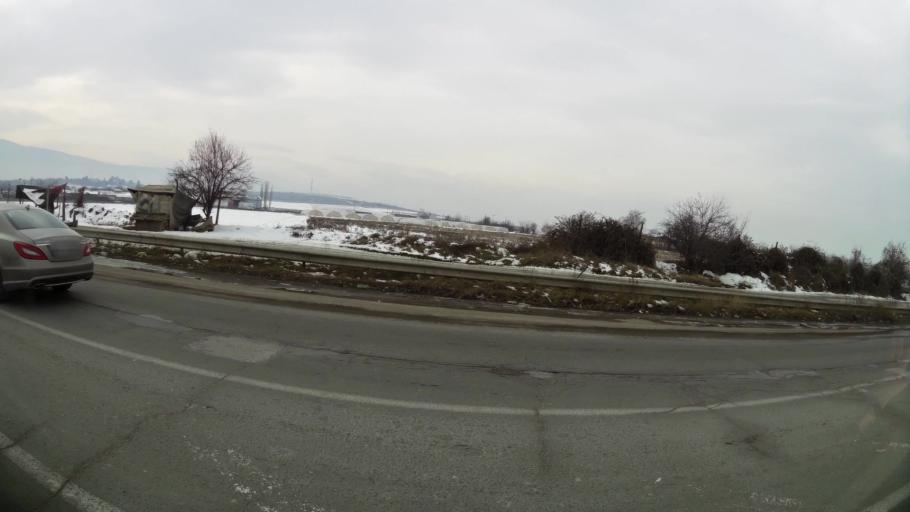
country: MK
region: Suto Orizari
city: Suto Orizare
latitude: 42.0247
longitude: 21.4090
